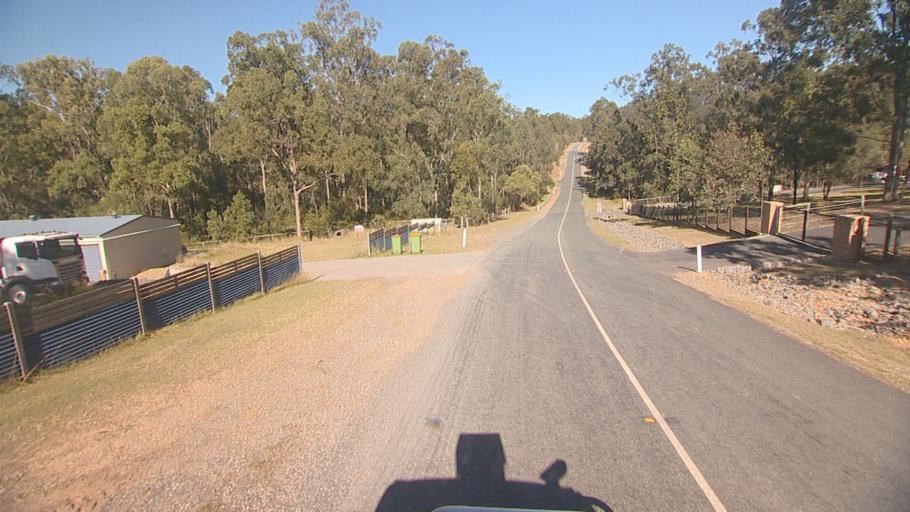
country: AU
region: Queensland
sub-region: Ipswich
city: Springfield Lakes
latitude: -27.7164
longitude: 152.9160
